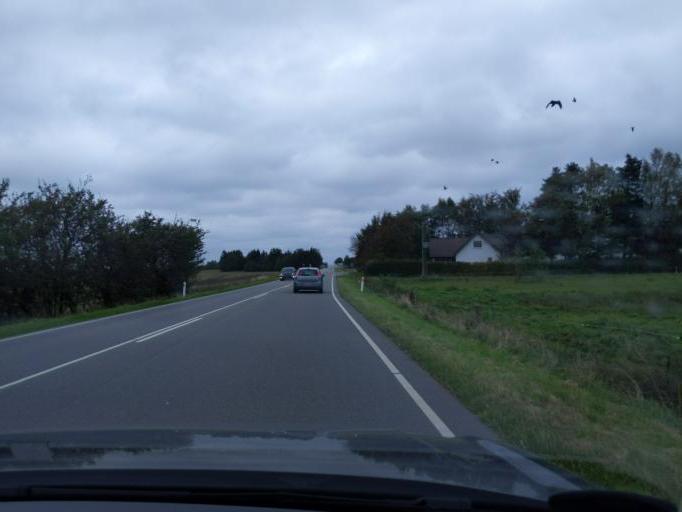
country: DK
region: North Denmark
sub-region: Mariagerfjord Kommune
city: Hobro
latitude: 56.5754
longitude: 9.8152
